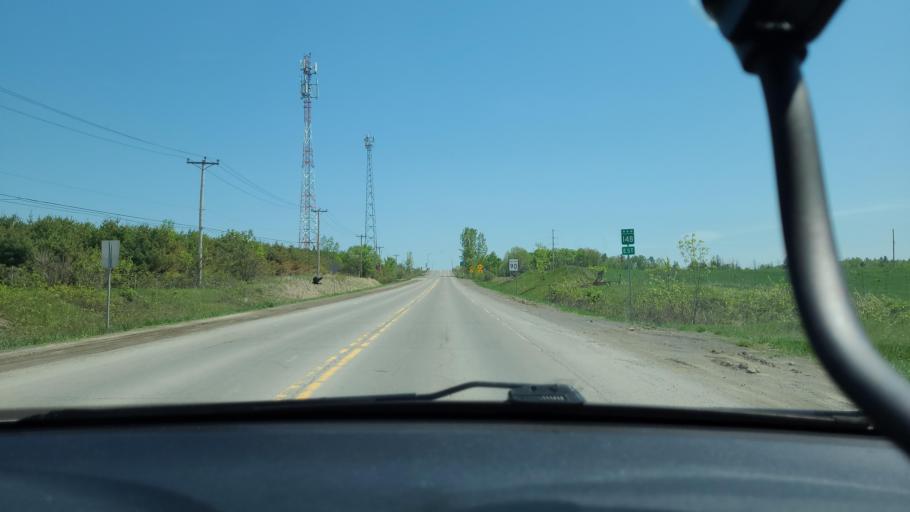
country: CA
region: Quebec
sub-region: Laurentides
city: Saint-Colomban
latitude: 45.6788
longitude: -74.1890
